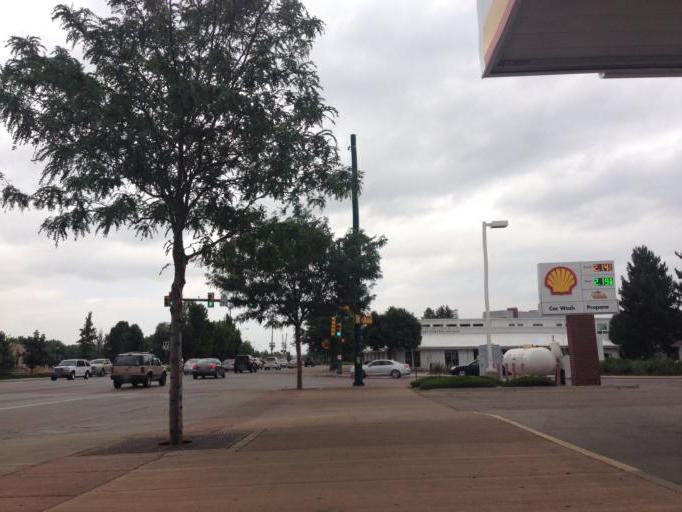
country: US
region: Colorado
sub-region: Larimer County
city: Fort Collins
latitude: 40.5918
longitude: -105.0767
